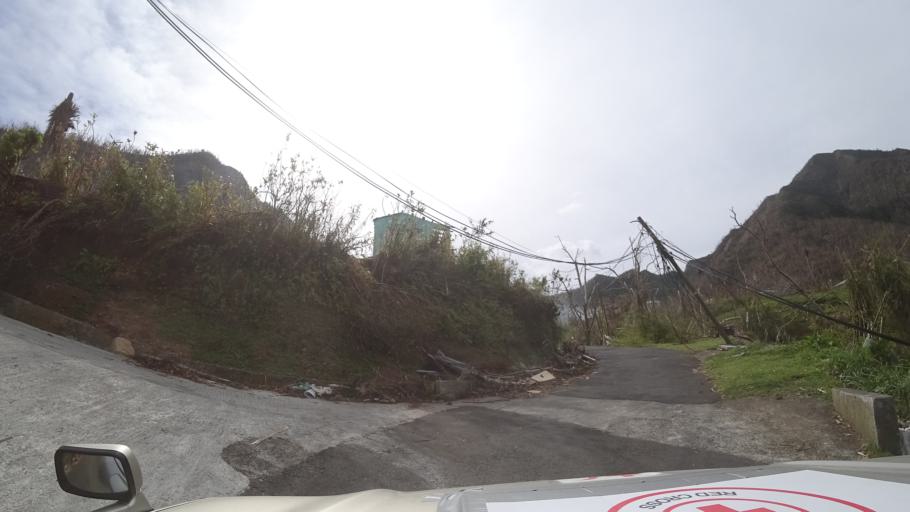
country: DM
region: Saint Patrick
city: Berekua
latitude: 15.2359
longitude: -61.3339
